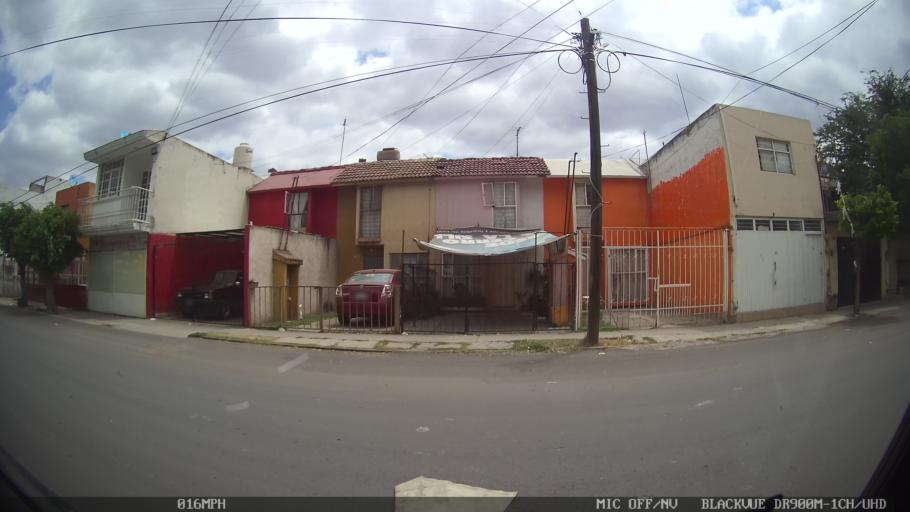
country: MX
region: Jalisco
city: Tonala
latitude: 20.6370
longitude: -103.2625
